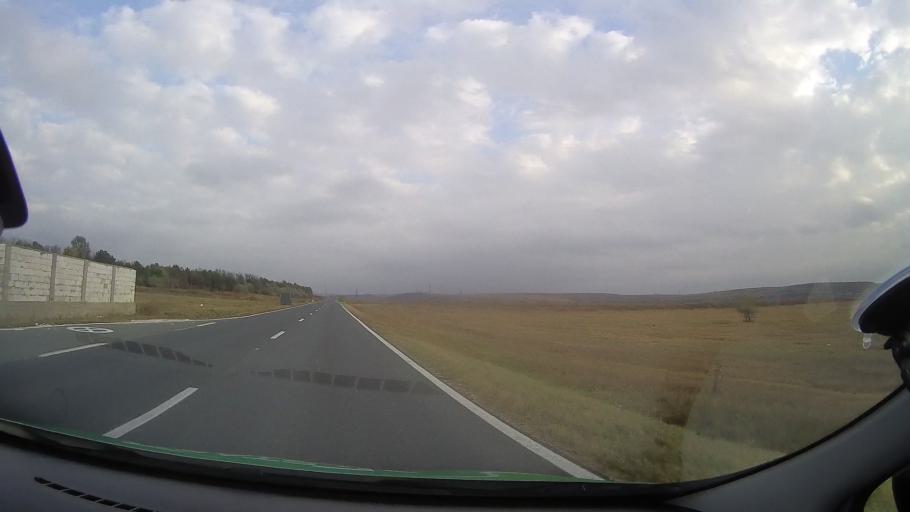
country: RO
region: Constanta
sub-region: Comuna Mircea Voda
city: Mircea Voda
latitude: 44.2702
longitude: 28.1747
